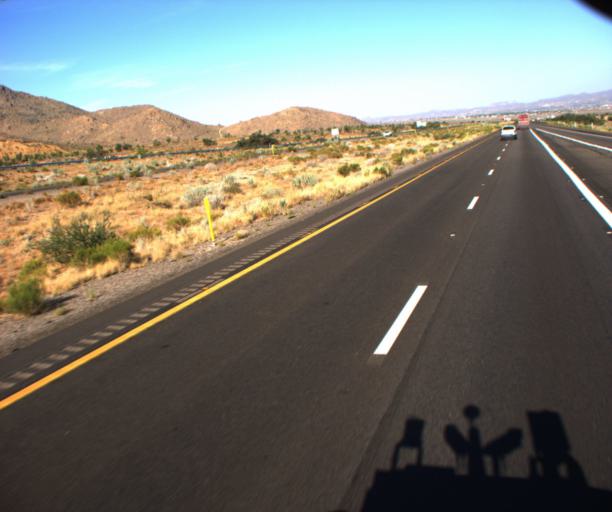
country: US
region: Arizona
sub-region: Mohave County
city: New Kingman-Butler
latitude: 35.1981
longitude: -113.9096
